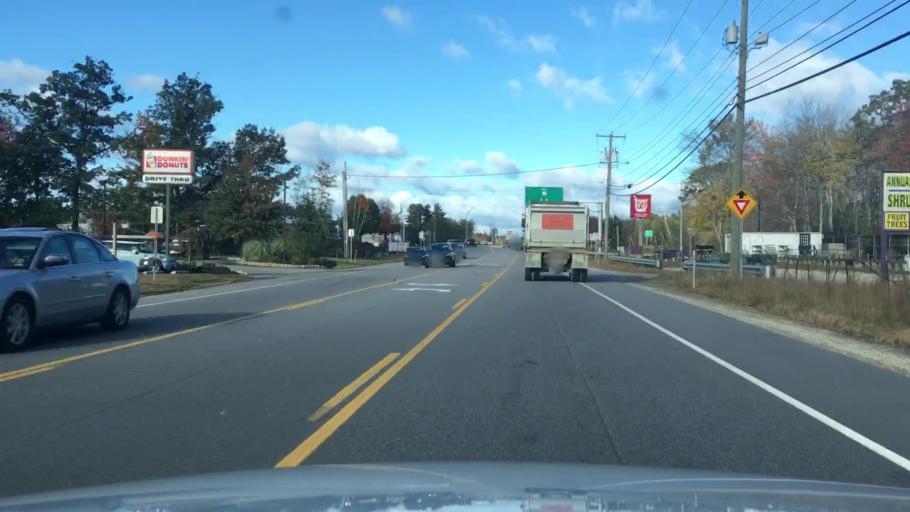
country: US
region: New Hampshire
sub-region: Strafford County
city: Lee
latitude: 43.1488
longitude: -71.0038
